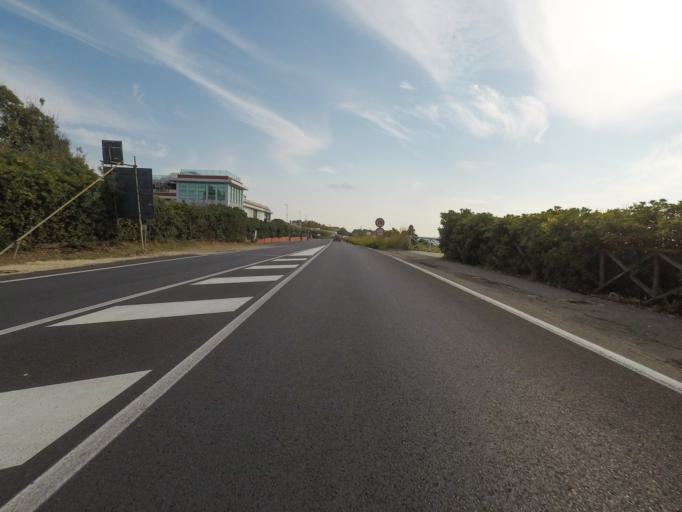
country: IT
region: Latium
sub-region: Citta metropolitana di Roma Capitale
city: Civitavecchia
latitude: 42.0543
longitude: 11.8201
